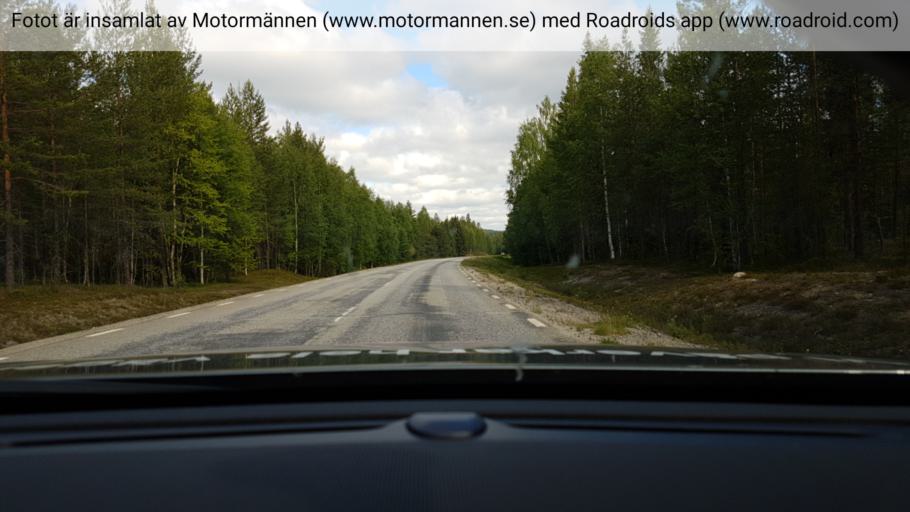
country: SE
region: Vaesterbotten
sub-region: Lycksele Kommun
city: Lycksele
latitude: 64.8433
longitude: 18.7626
